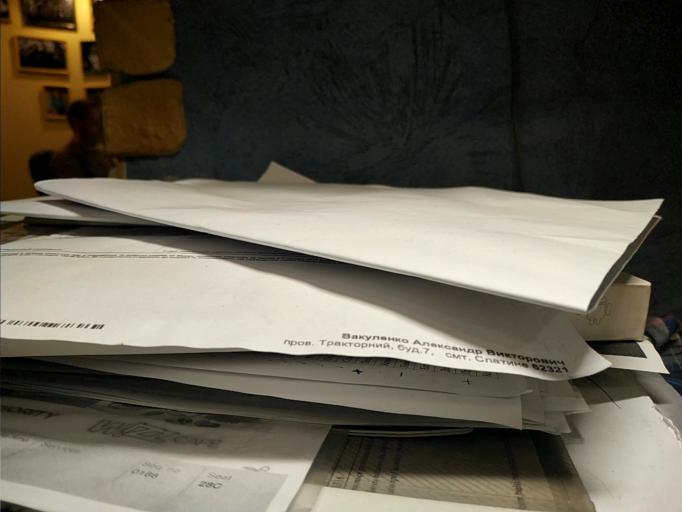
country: RU
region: Tverskaya
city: Zubtsov
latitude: 56.1162
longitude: 34.5961
